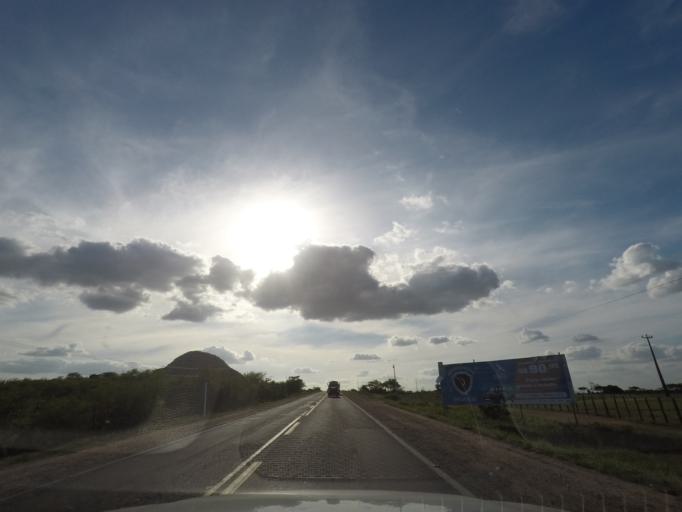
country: BR
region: Bahia
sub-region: Anguera
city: Anguera
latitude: -12.1815
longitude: -39.4570
